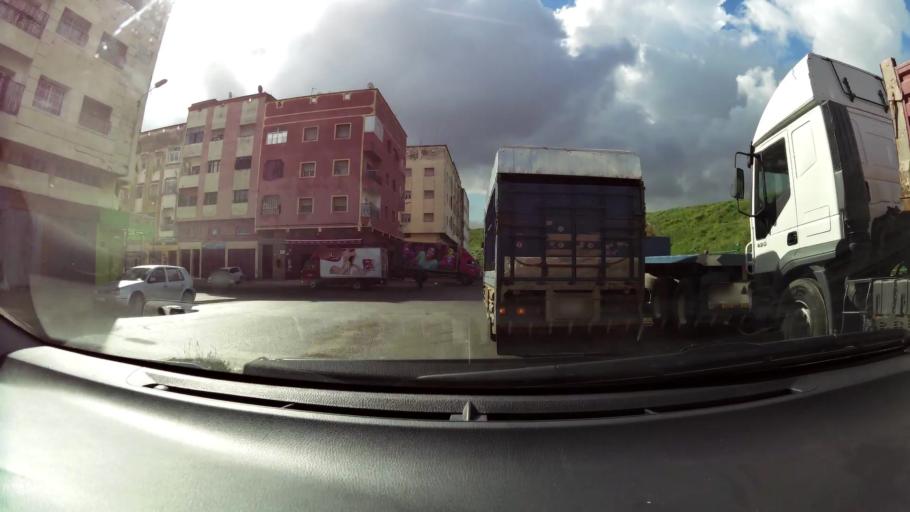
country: MA
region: Grand Casablanca
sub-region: Mediouna
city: Tit Mellil
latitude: 33.5771
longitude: -7.5345
